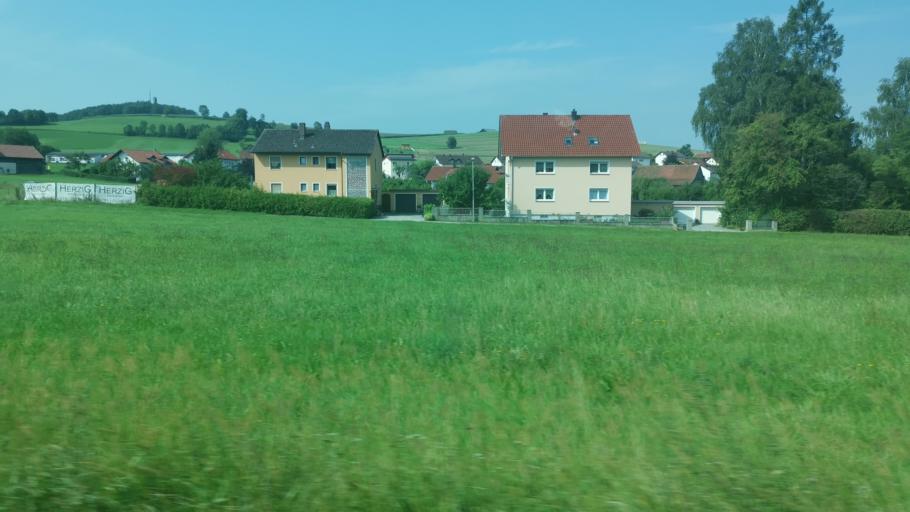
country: DE
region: Bavaria
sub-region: Upper Palatinate
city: Willmering
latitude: 49.2393
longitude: 12.6753
